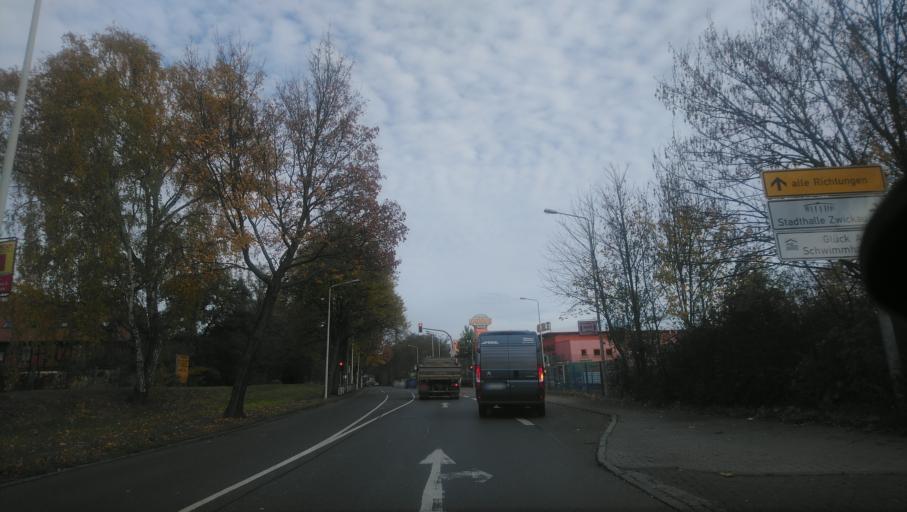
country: DE
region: Saxony
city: Zwickau
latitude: 50.7048
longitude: 12.4936
